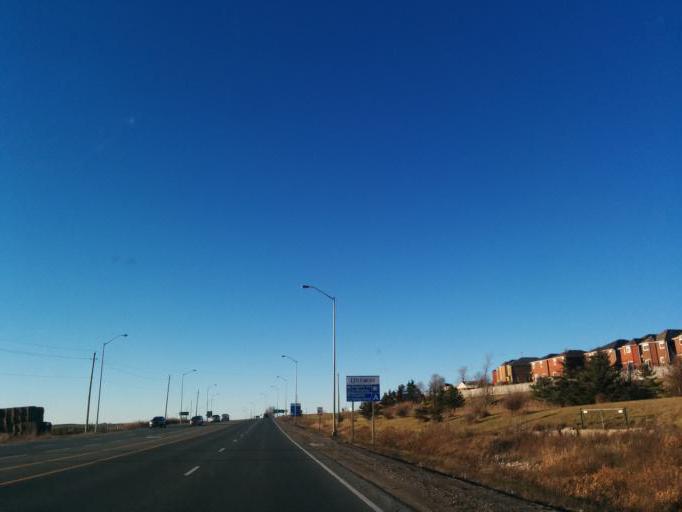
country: CA
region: Ontario
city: Orangeville
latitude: 43.9161
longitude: -80.0720
